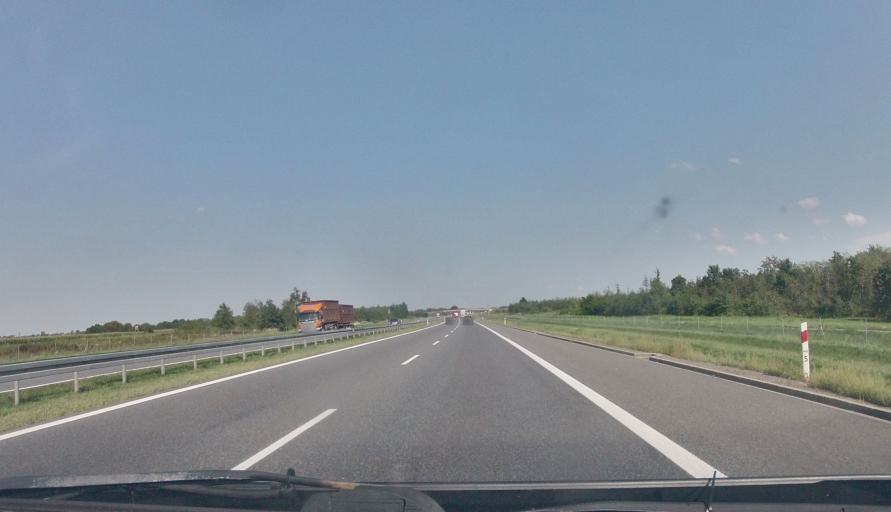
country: PL
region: Lesser Poland Voivodeship
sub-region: Powiat bochenski
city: Krzeczow
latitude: 50.0043
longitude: 20.4890
